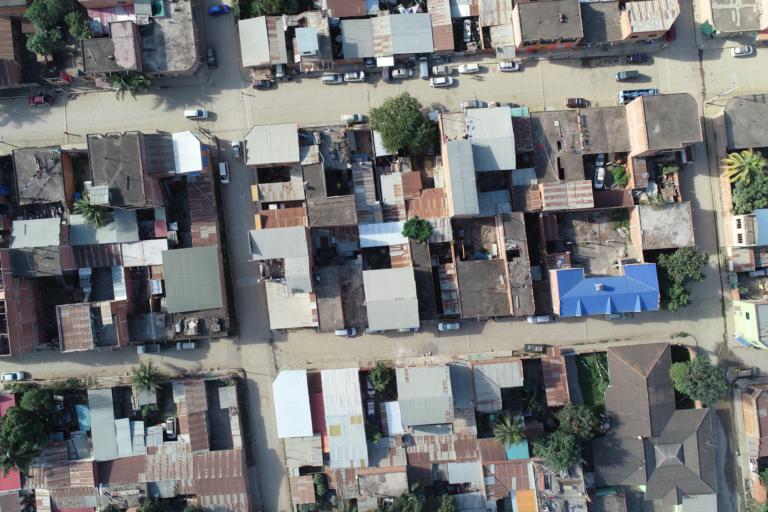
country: BO
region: La Paz
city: Coroico
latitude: -15.8366
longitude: -67.5611
